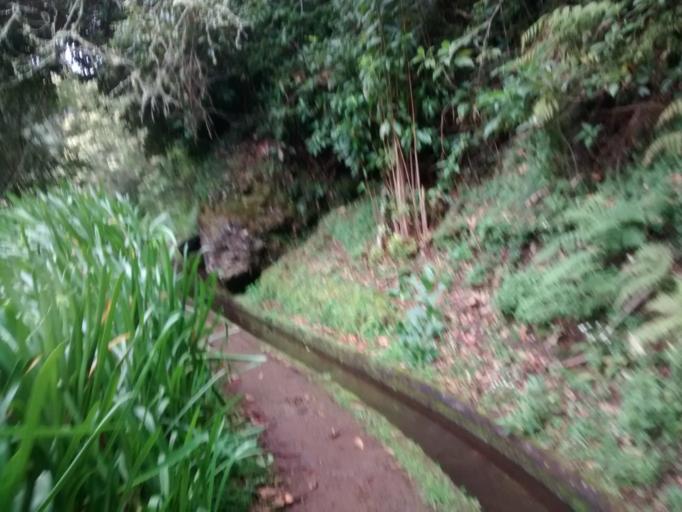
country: PT
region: Madeira
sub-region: Santana
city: Santana
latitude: 32.8146
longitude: -16.9274
